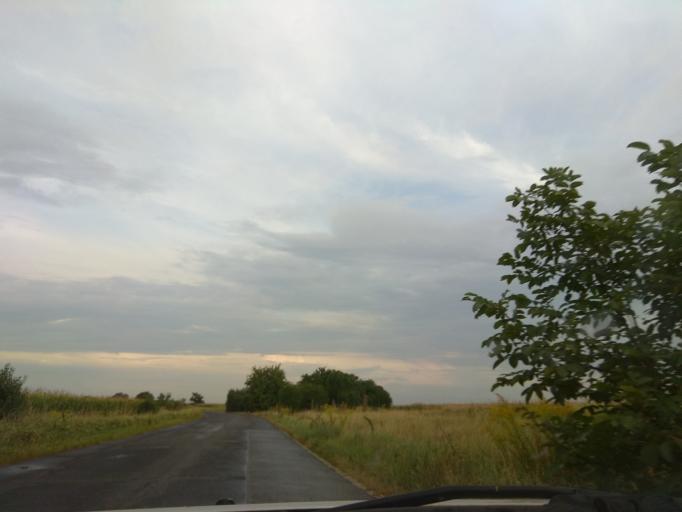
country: HU
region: Borsod-Abauj-Zemplen
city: Felsozsolca
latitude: 48.0947
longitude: 20.8324
